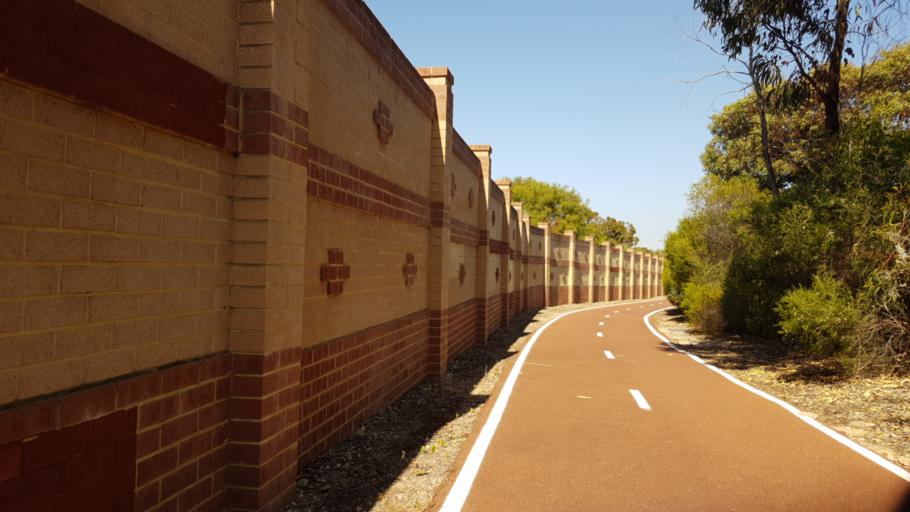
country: AU
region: Western Australia
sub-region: Stirling
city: Karrinyup
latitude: -31.8560
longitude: 115.7798
